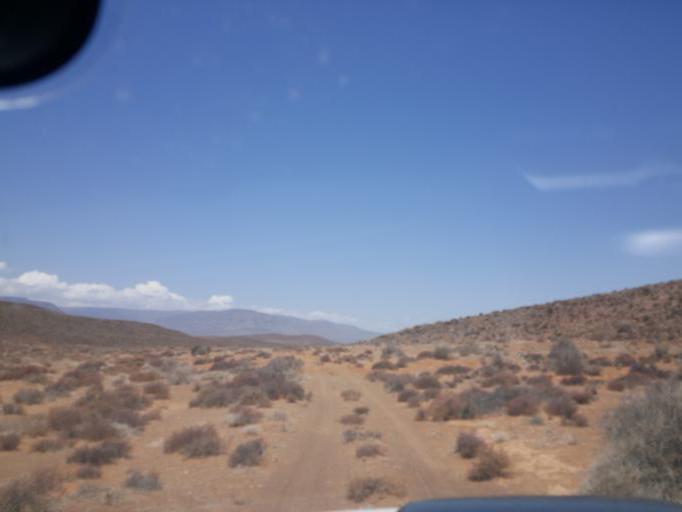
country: ZA
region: Northern Cape
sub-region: Namakwa District Municipality
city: Calvinia
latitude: -32.1993
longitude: 20.0048
